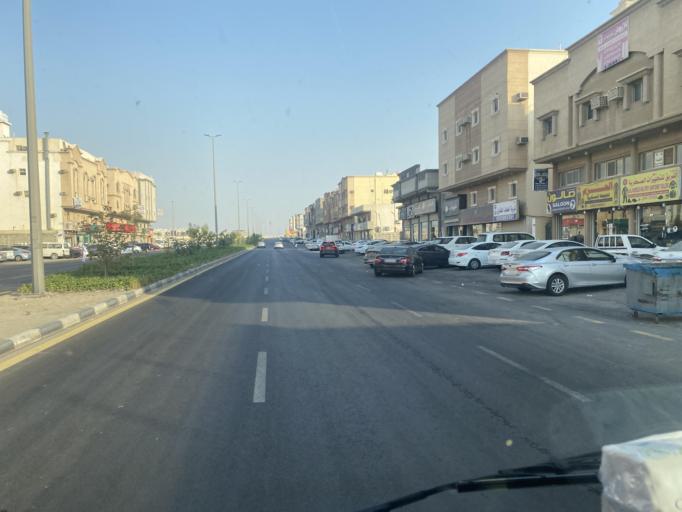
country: SA
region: Eastern Province
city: Dhahran
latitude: 26.3541
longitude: 50.0482
